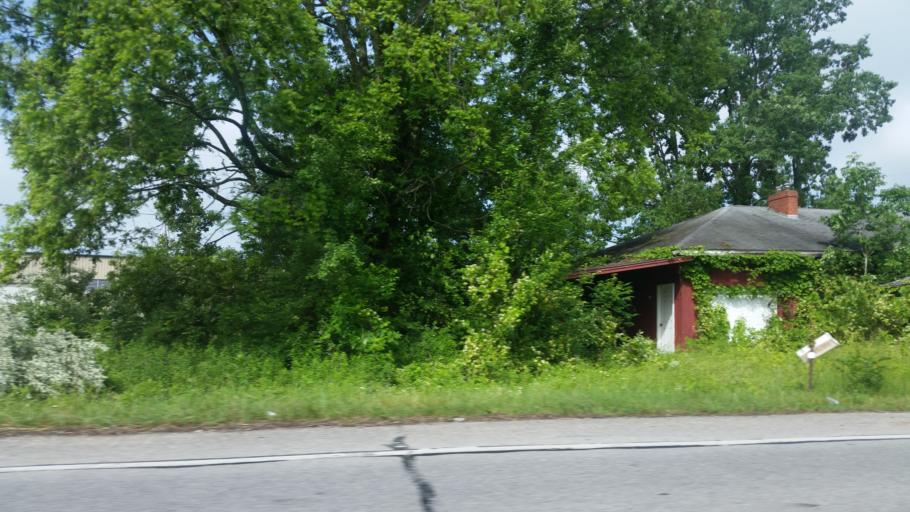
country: US
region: Kentucky
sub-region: Rowan County
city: Morehead
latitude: 38.2115
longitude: -83.4783
